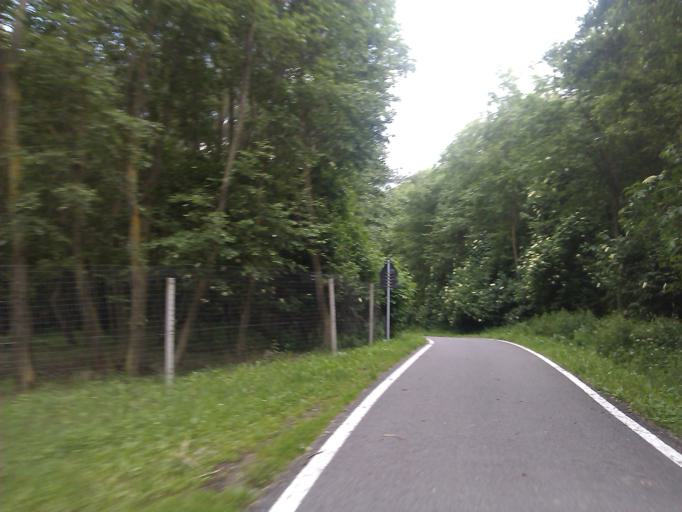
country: IT
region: Trentino-Alto Adige
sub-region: Bolzano
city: Prato Allo Stelvio
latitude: 46.6385
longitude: 10.5982
